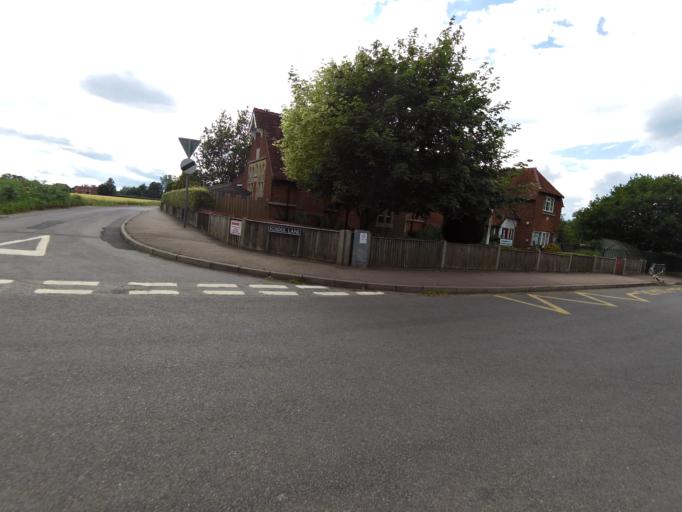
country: GB
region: England
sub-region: Norfolk
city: Ditchingham
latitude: 52.4780
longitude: 1.4816
